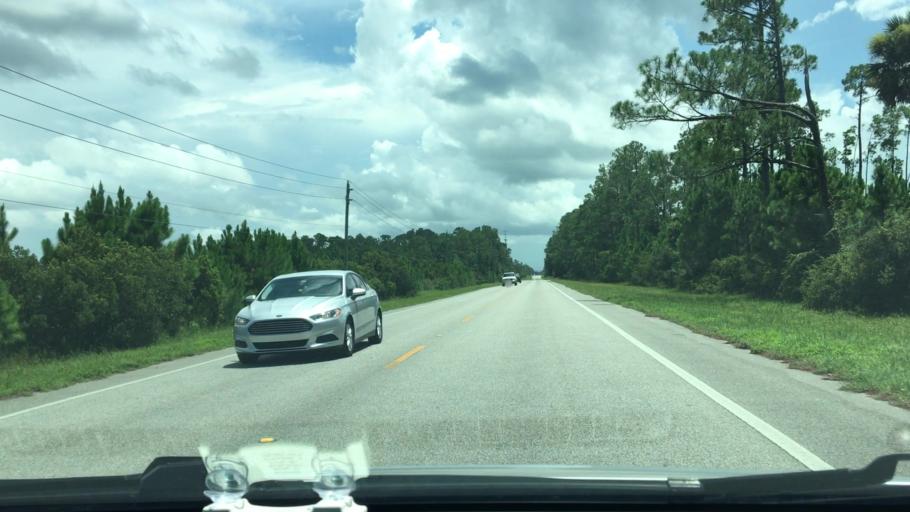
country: US
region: Florida
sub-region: Volusia County
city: Samsula-Spruce Creek
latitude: 29.0227
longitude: -81.0671
